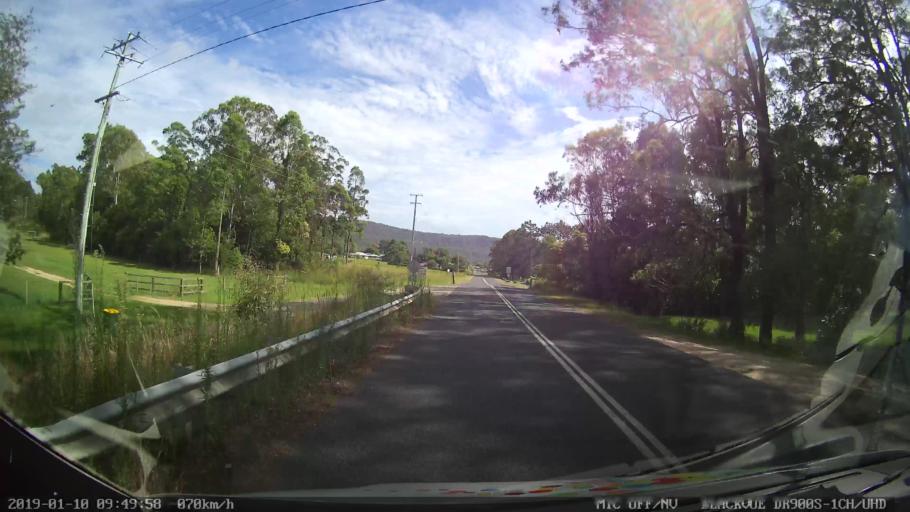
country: AU
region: New South Wales
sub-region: Coffs Harbour
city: Nana Glen
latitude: -30.0573
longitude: 152.9774
